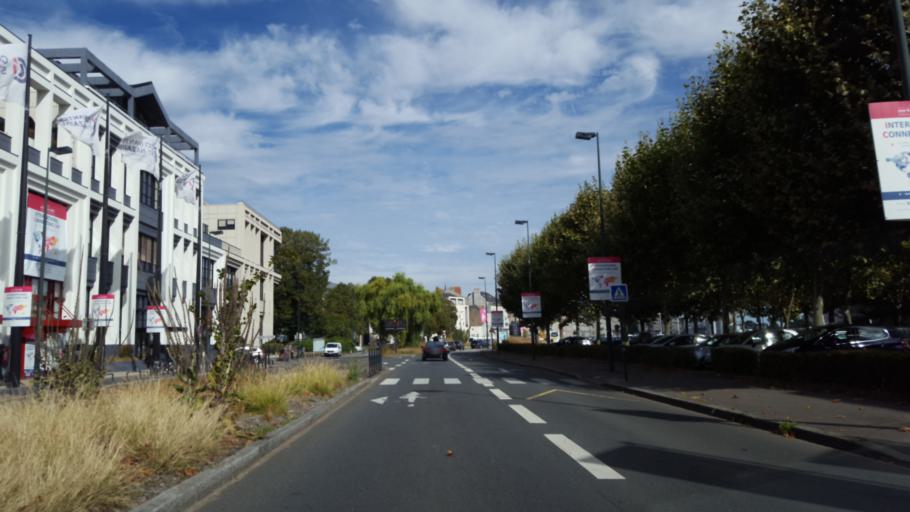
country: FR
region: Pays de la Loire
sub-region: Departement de la Loire-Atlantique
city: Nantes
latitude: 47.2057
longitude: -1.5740
